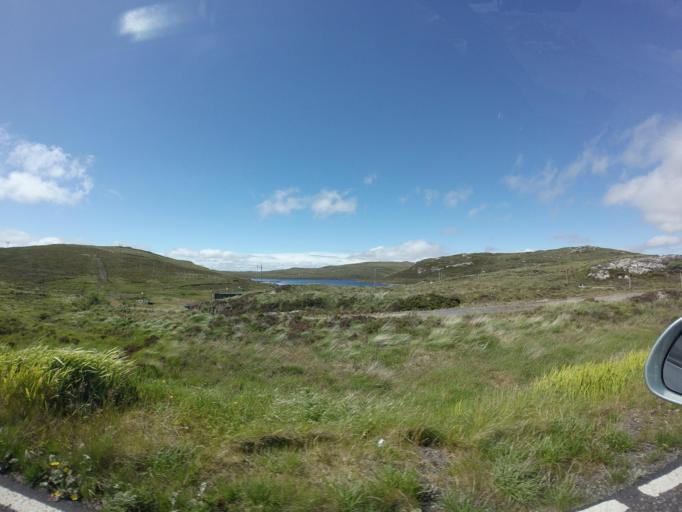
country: GB
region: Scotland
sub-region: Eilean Siar
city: Stornoway
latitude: 58.1244
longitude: -6.5077
